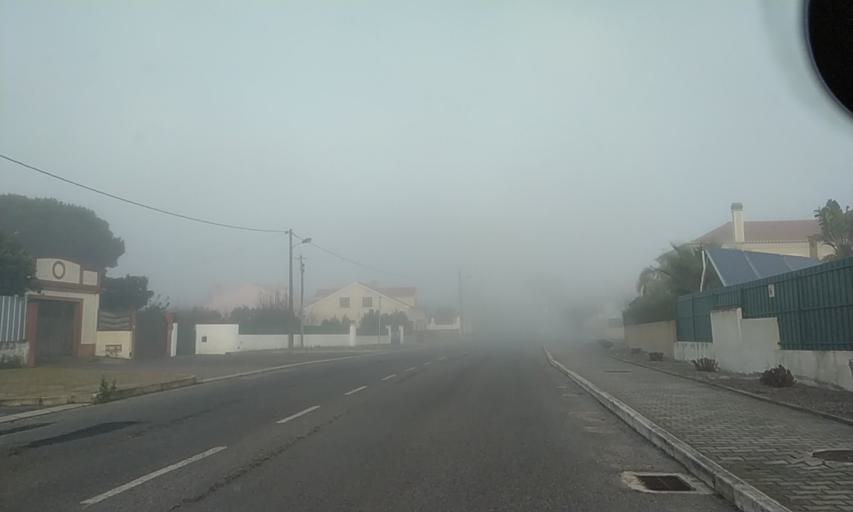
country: PT
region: Setubal
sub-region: Setubal
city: Setubal
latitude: 38.5417
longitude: -8.8491
